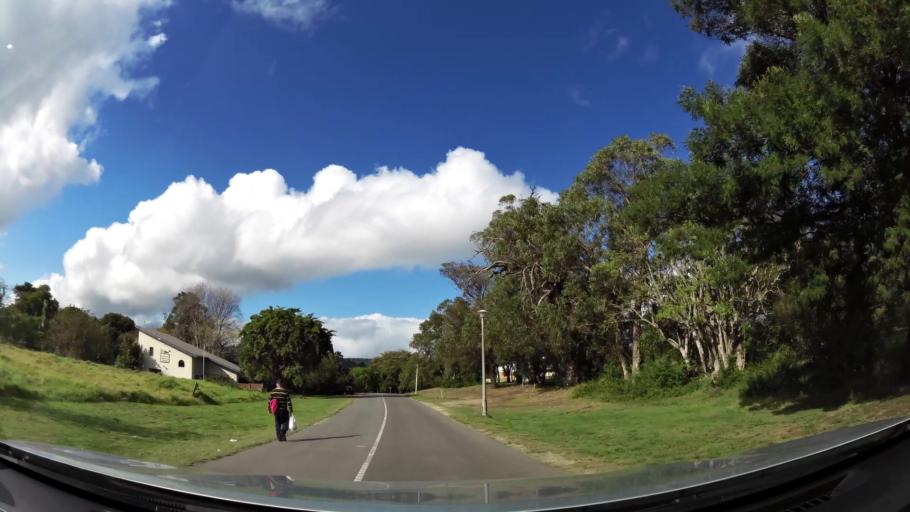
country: ZA
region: Western Cape
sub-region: Eden District Municipality
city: Knysna
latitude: -34.0413
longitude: 23.0722
